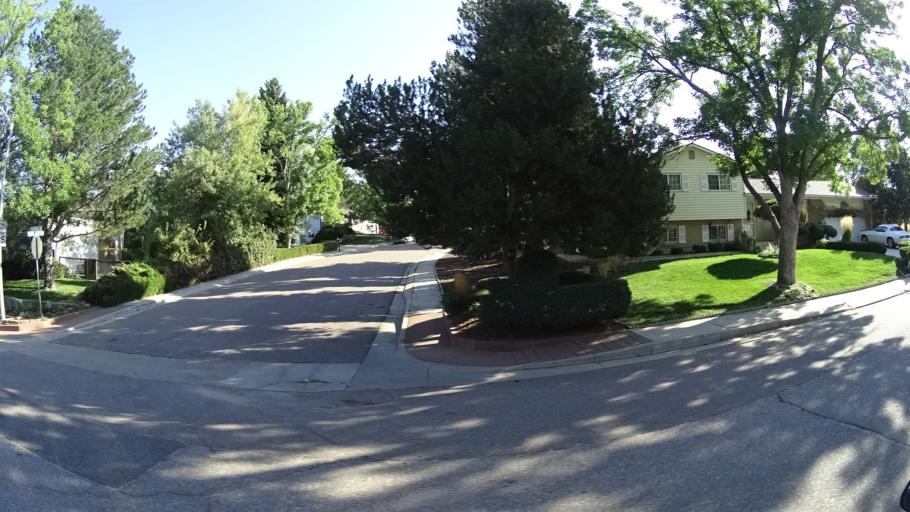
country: US
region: Colorado
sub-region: El Paso County
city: Cimarron Hills
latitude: 38.8787
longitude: -104.7352
